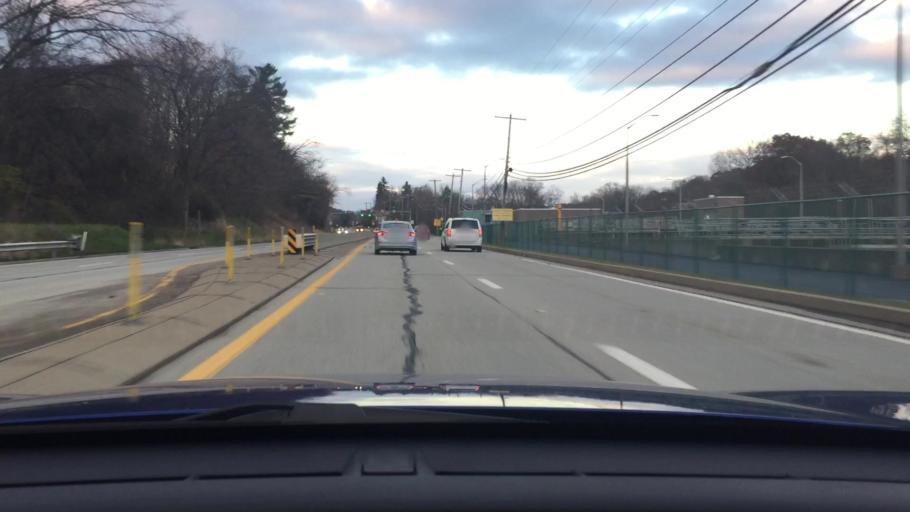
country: US
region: Pennsylvania
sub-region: Westmoreland County
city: South Greensburg
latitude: 40.2671
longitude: -79.5607
